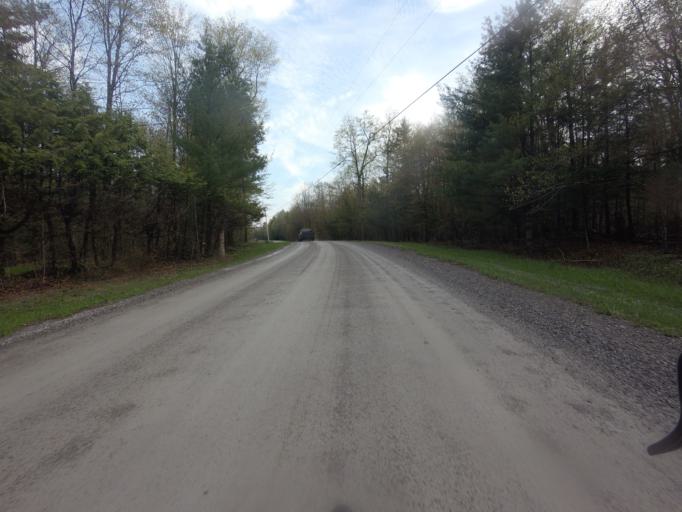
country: CA
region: Ontario
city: Carleton Place
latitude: 45.1988
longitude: -76.3272
